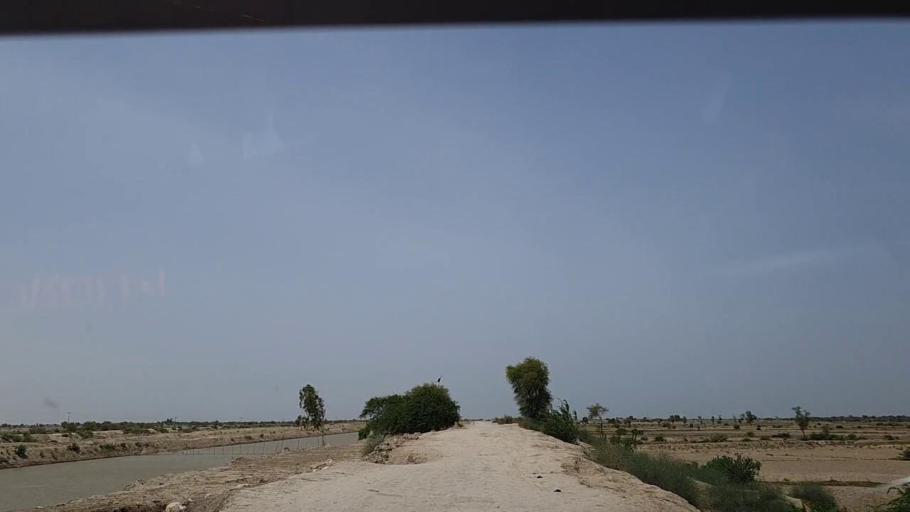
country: PK
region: Sindh
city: Johi
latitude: 26.7295
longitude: 67.6819
